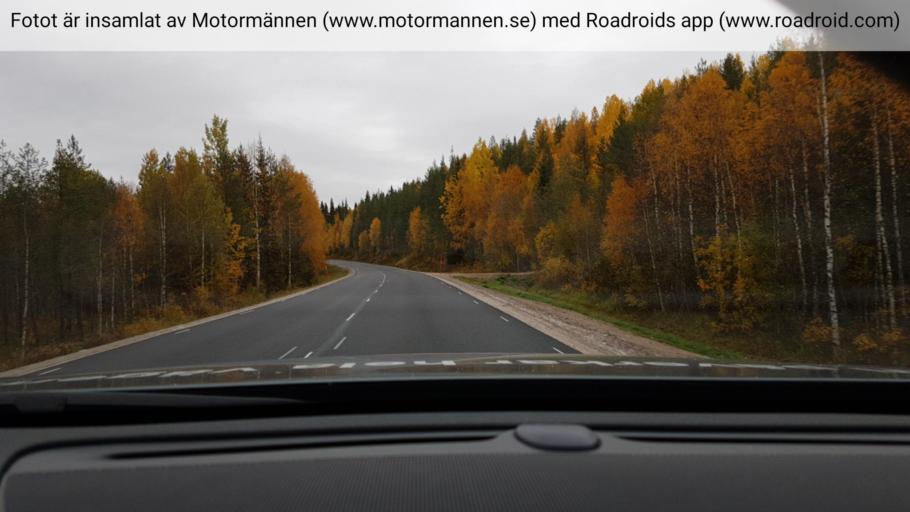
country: SE
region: Norrbotten
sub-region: Overkalix Kommun
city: OEverkalix
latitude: 66.4610
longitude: 22.7921
